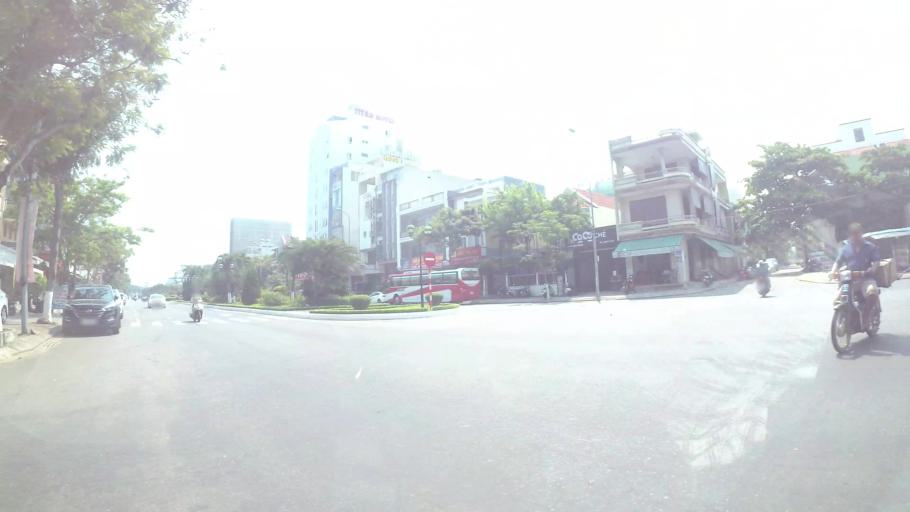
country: VN
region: Da Nang
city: Ngu Hanh Son
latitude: 16.0397
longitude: 108.2458
